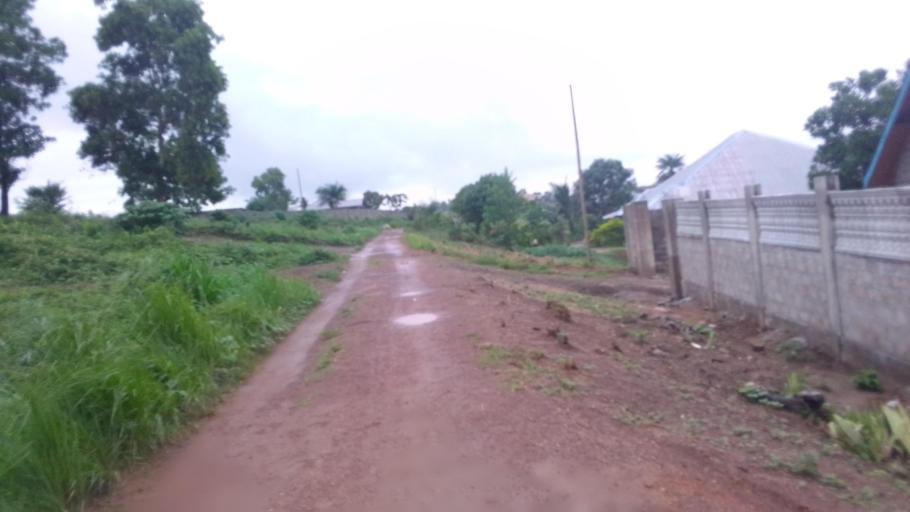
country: SL
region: Eastern Province
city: Kenema
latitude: 7.9032
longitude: -11.1605
